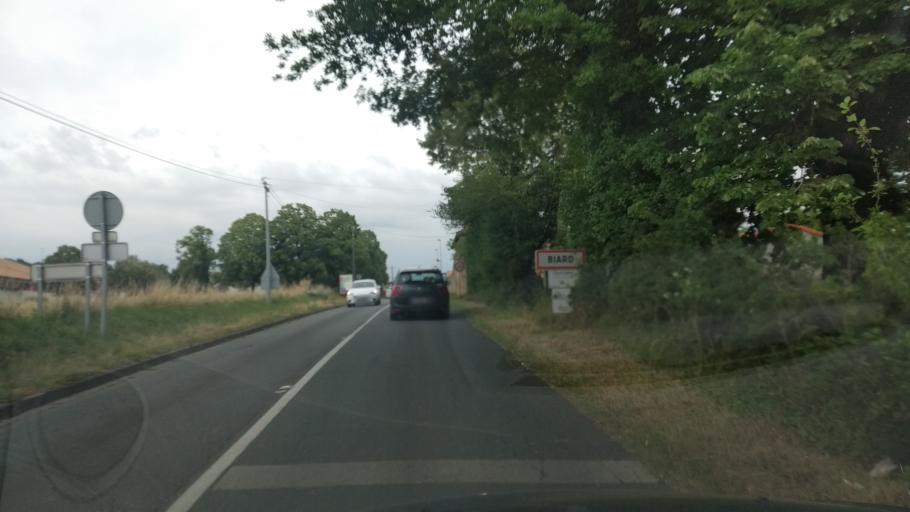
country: FR
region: Poitou-Charentes
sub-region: Departement de la Vienne
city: Biard
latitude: 46.5764
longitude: 0.3027
